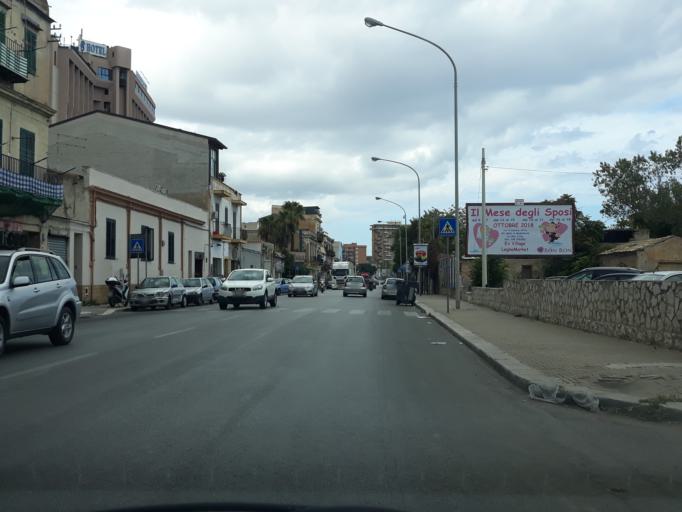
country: IT
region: Sicily
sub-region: Palermo
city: Ciaculli
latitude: 38.1071
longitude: 13.3826
